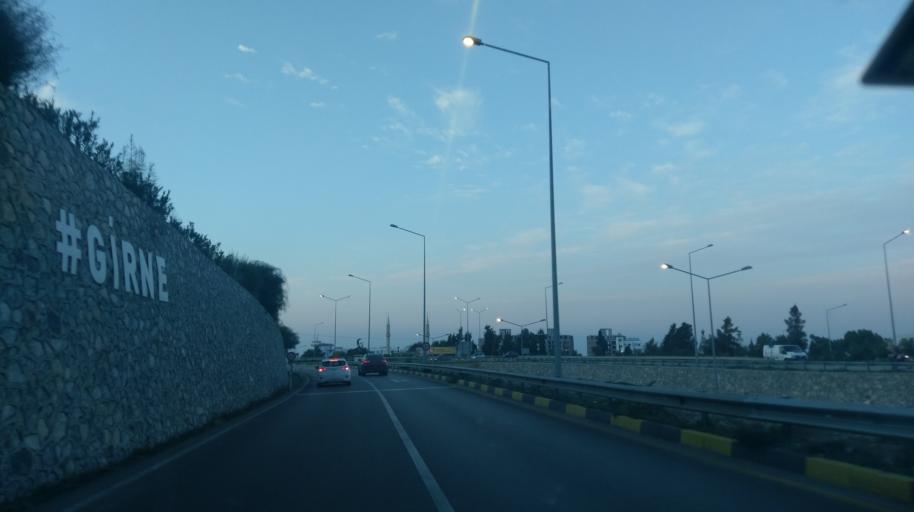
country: CY
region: Keryneia
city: Kyrenia
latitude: 35.3239
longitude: 33.3177
